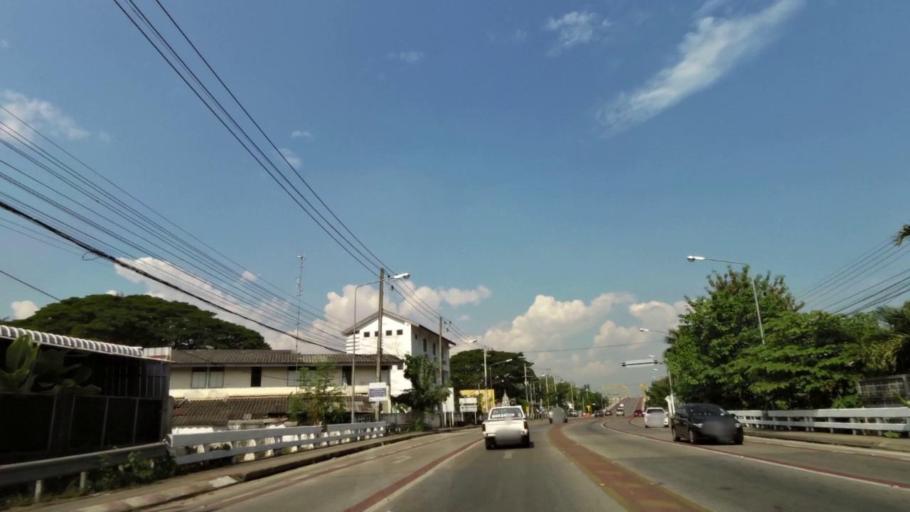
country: TH
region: Chiang Rai
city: Chiang Rai
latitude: 19.9140
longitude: 99.8323
